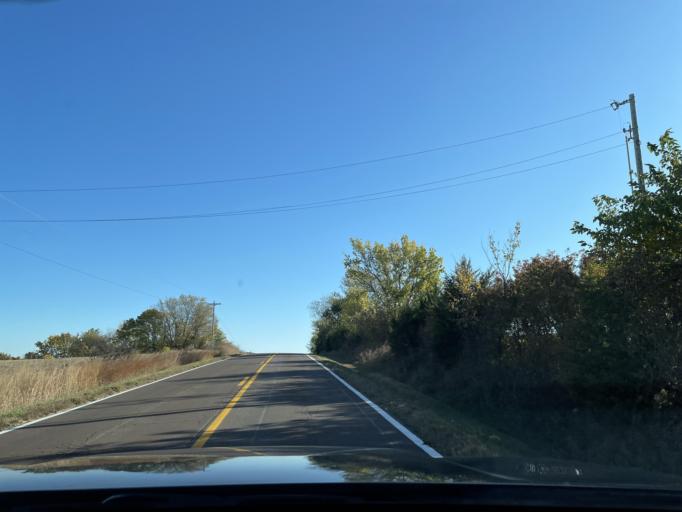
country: US
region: Missouri
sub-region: Andrew County
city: Savannah
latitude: 39.9201
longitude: -94.8673
